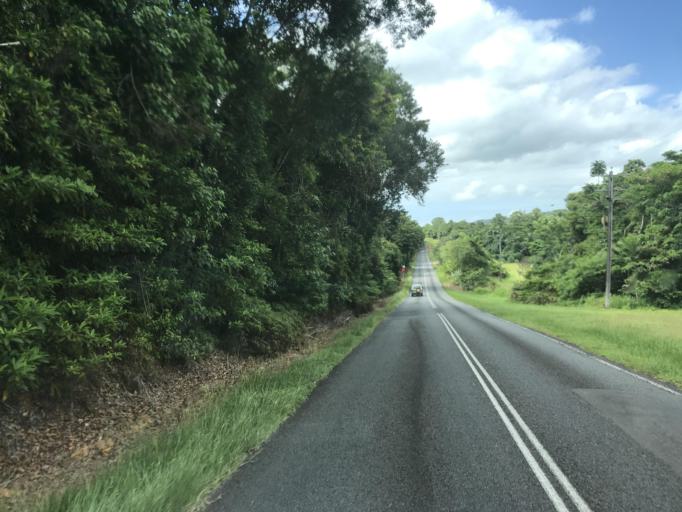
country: AU
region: Queensland
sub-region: Cassowary Coast
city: Innisfail
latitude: -17.8322
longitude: 146.0537
